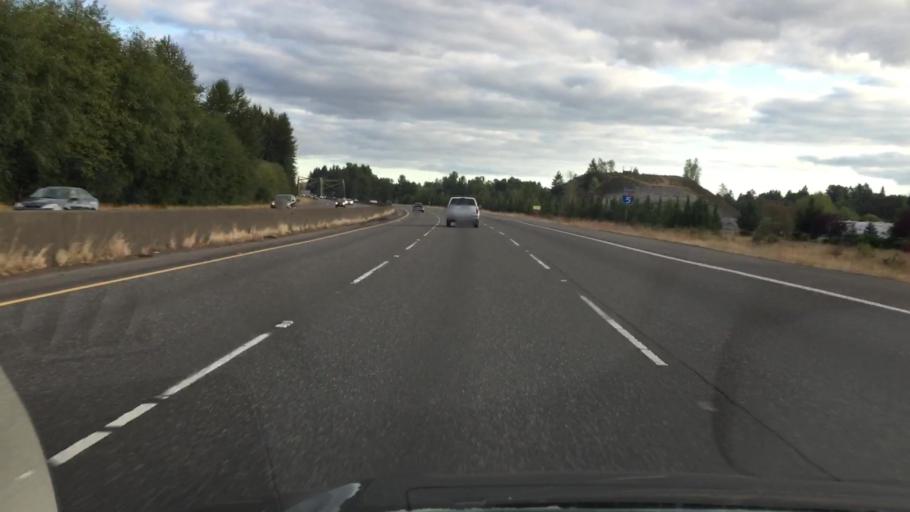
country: US
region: Washington
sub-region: Cowlitz County
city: Castle Rock
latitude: 46.3175
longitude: -122.9152
